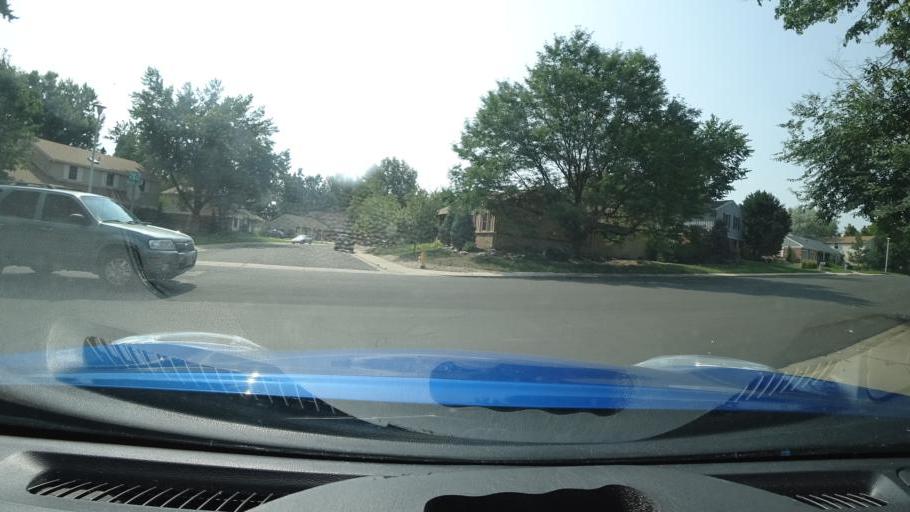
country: US
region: Colorado
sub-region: Adams County
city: Aurora
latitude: 39.6656
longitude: -104.8550
